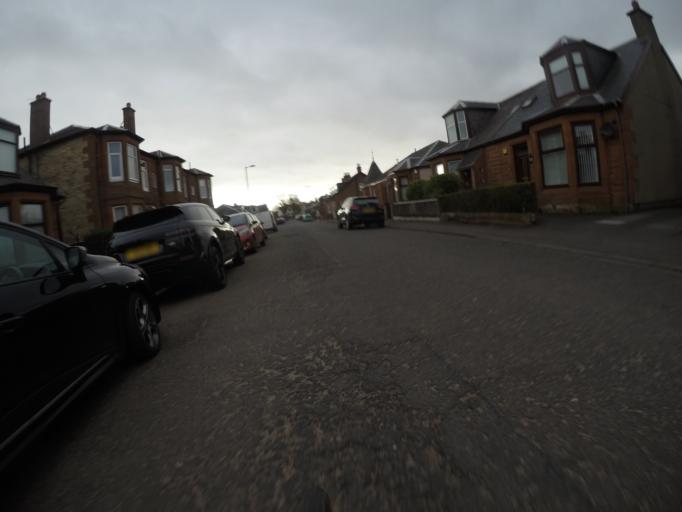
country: GB
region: Scotland
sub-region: East Ayrshire
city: Kilmarnock
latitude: 55.6163
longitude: -4.4862
